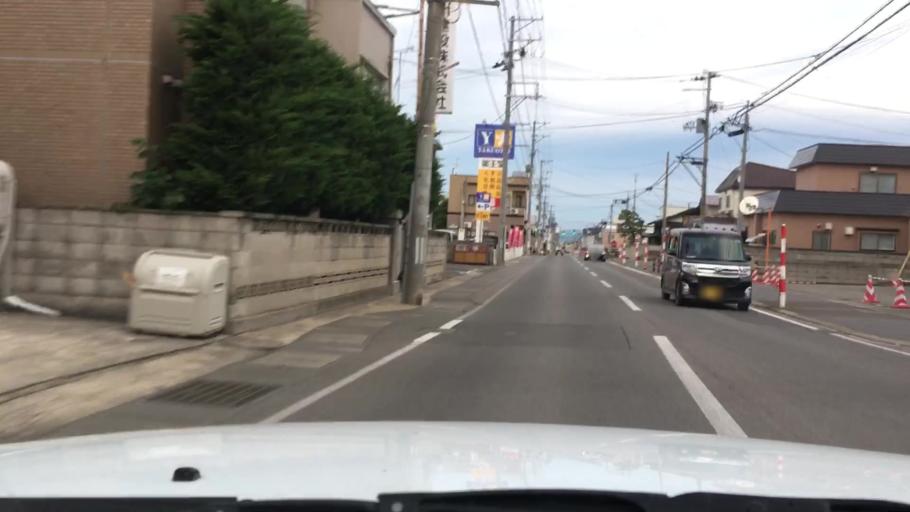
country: JP
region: Aomori
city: Hirosaki
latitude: 40.5859
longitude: 140.4757
